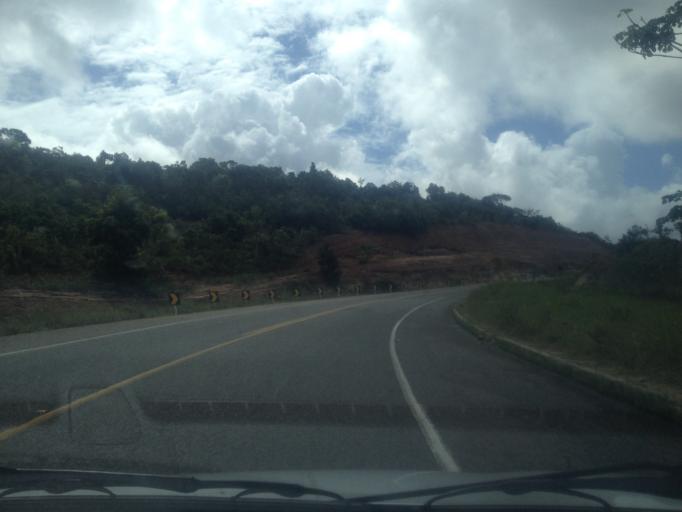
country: BR
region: Bahia
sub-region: Conde
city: Conde
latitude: -12.0854
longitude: -37.7722
